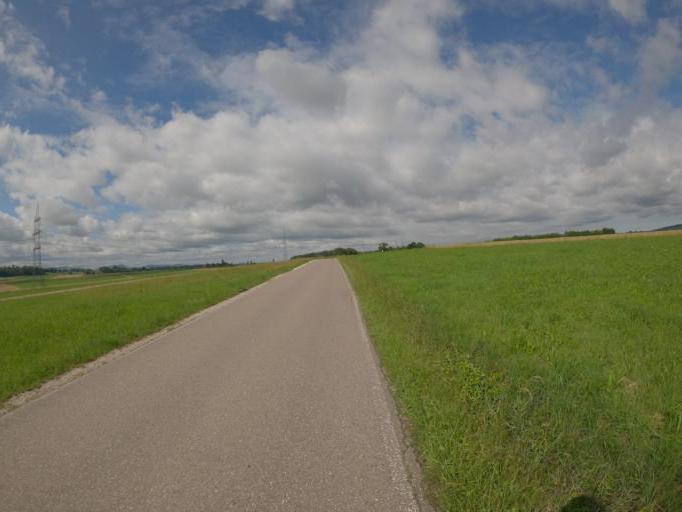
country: DE
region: Baden-Wuerttemberg
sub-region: Regierungsbezirk Stuttgart
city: Ebersbach an der Fils
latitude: 48.7031
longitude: 9.5189
